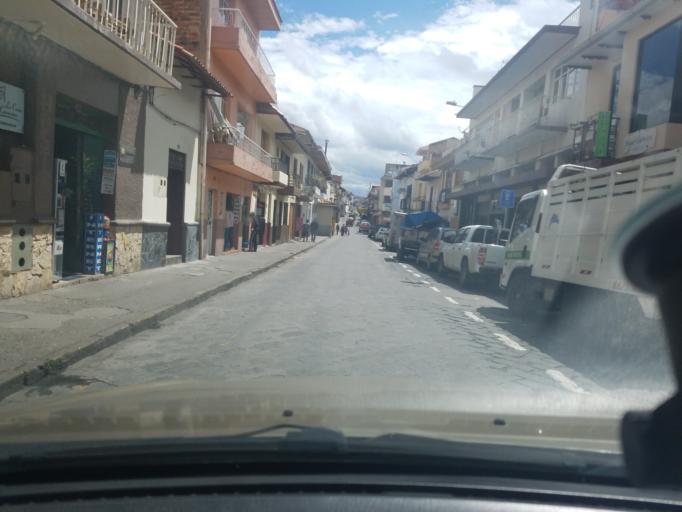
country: EC
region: Azuay
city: Cuenca
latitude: -2.9023
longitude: -79.0029
